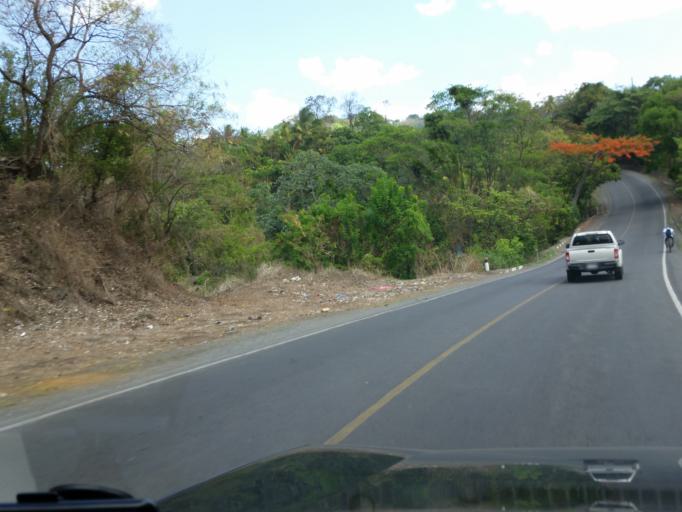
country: NI
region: Masaya
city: La Concepcion
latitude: 11.9578
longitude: -86.1913
